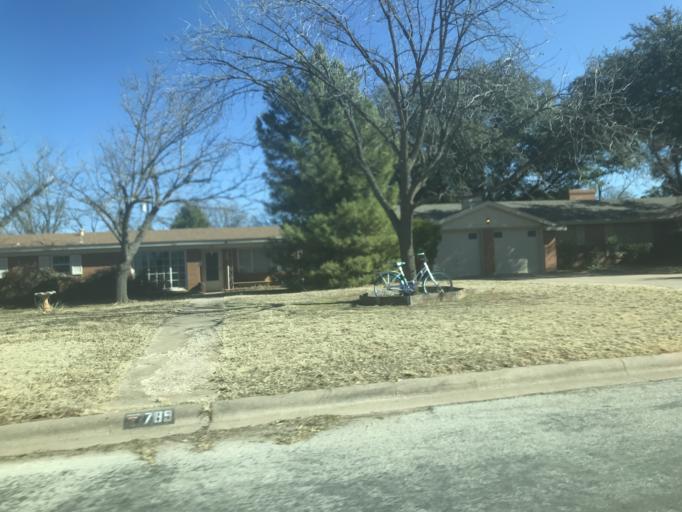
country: US
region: Texas
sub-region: Taylor County
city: Abilene
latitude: 32.4577
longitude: -99.7745
